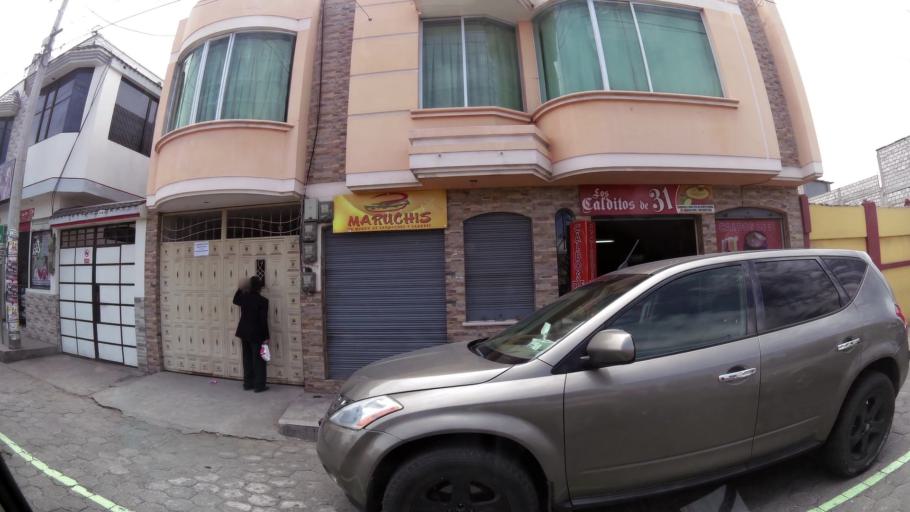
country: EC
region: Cotopaxi
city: San Miguel de Salcedo
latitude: -1.0453
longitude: -78.5875
